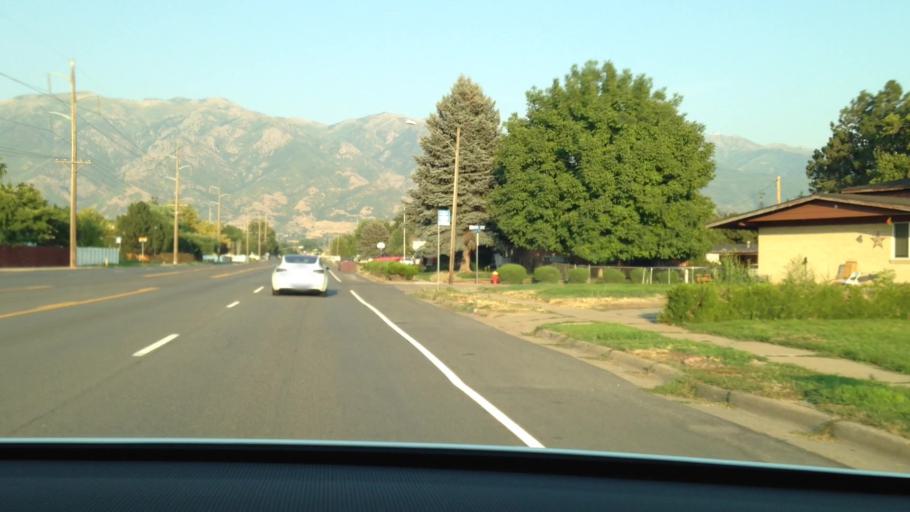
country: US
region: Utah
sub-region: Davis County
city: Layton
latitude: 41.0770
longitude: -111.9669
